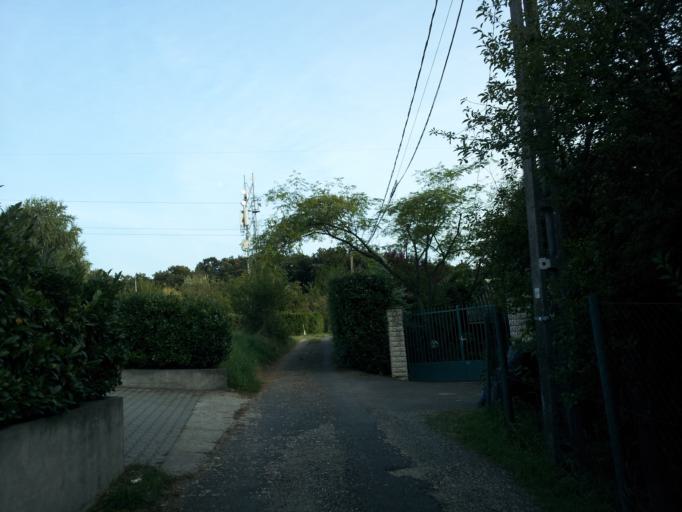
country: HU
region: Somogy
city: Zamardi
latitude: 46.8679
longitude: 17.9349
